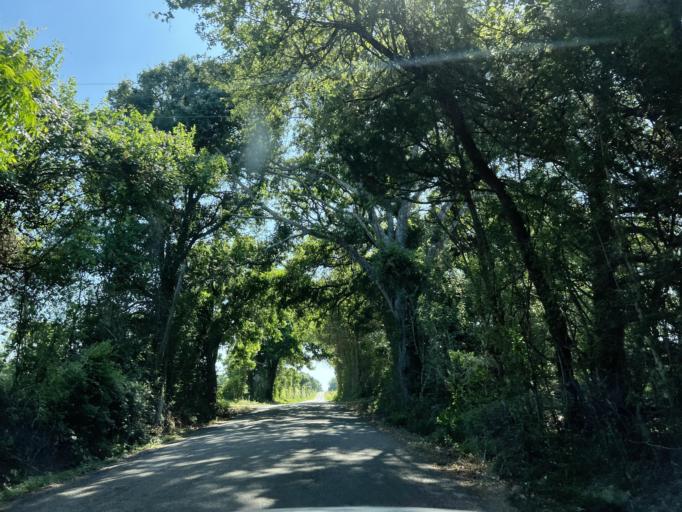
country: US
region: Texas
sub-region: Washington County
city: Brenham
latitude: 30.1550
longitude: -96.3577
